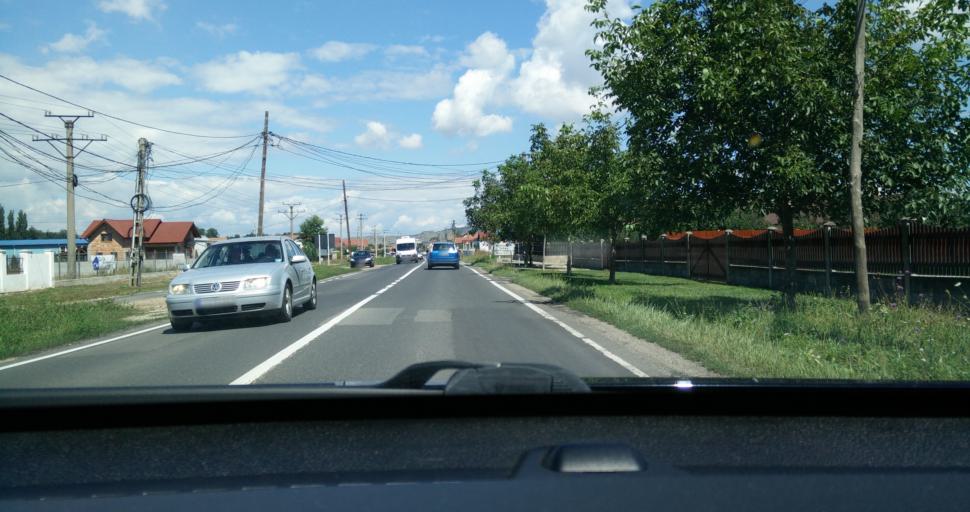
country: RO
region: Alba
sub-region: Municipiul Sebes
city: Petresti
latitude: 45.9380
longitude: 23.5625
